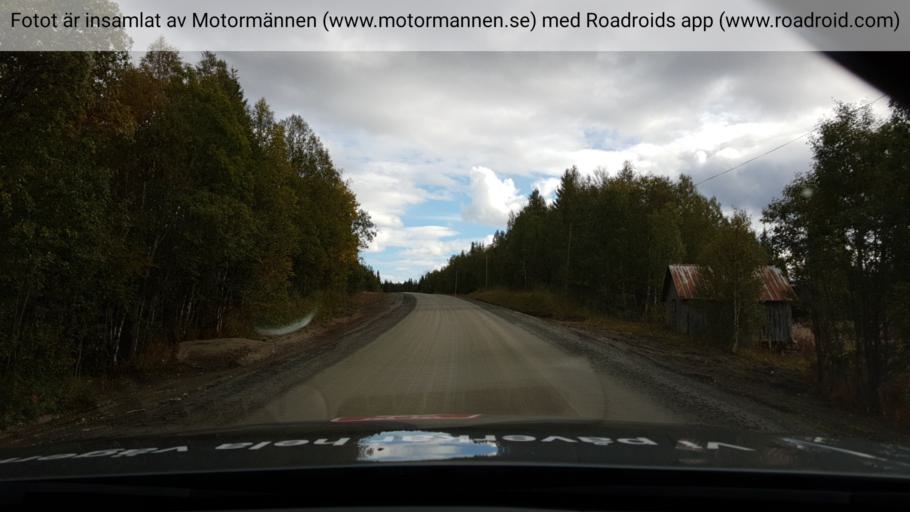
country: SE
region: Jaemtland
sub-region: Are Kommun
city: Are
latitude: 63.7048
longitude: 12.6554
